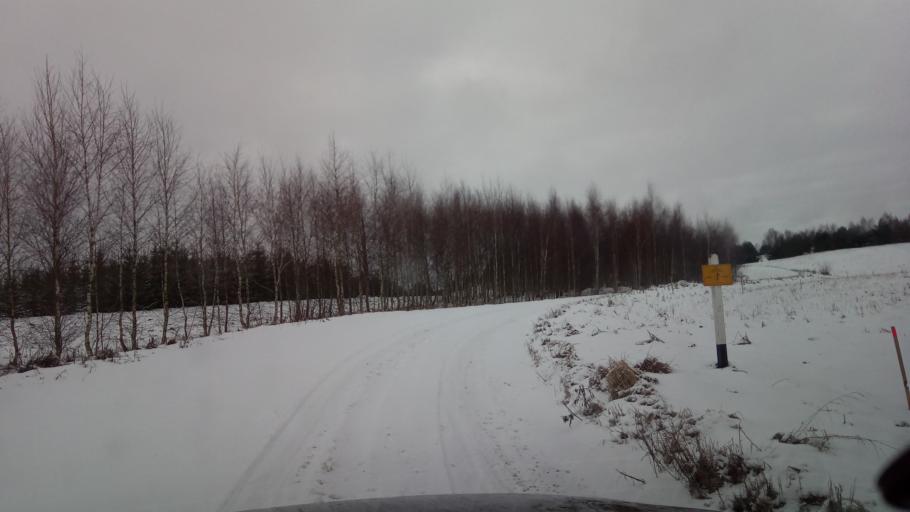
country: LT
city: Zarasai
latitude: 55.6827
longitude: 26.1067
